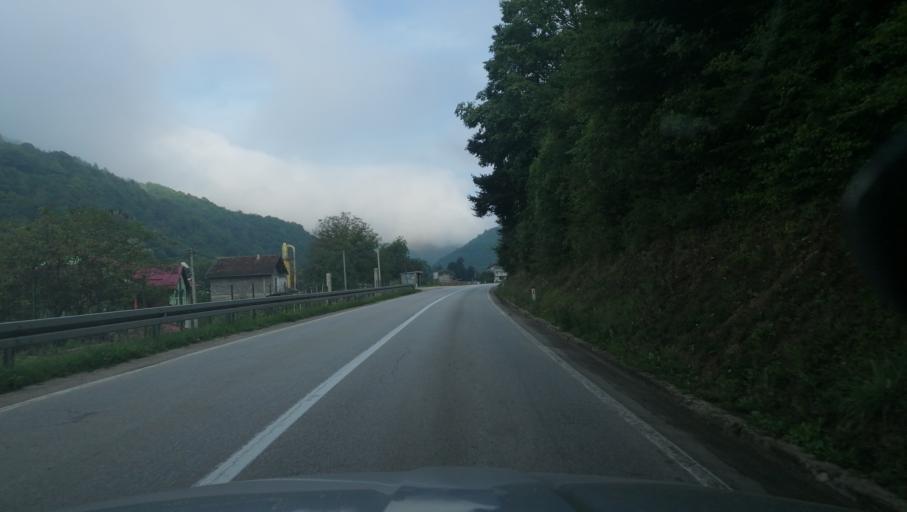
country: BA
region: Federation of Bosnia and Herzegovina
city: Donji Vakuf
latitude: 44.1752
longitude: 17.3575
